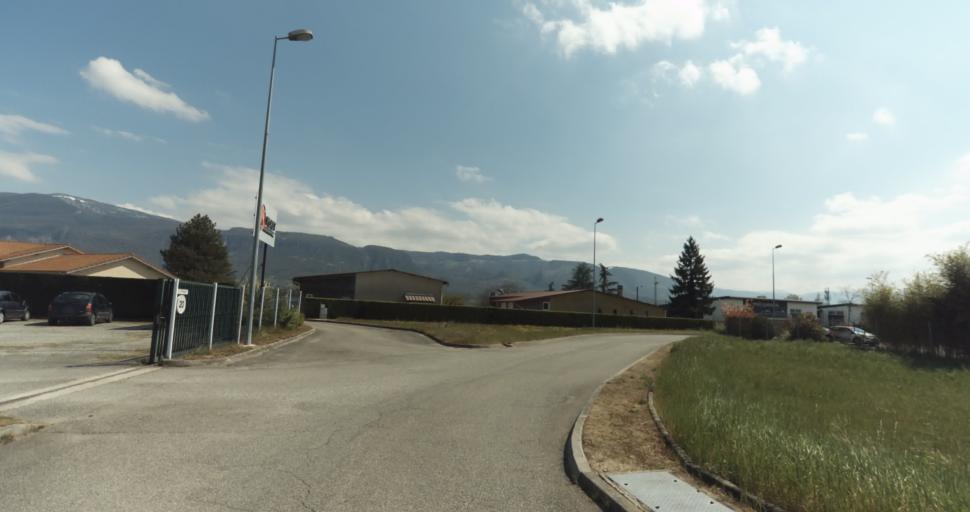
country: FR
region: Rhone-Alpes
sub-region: Departement de l'Isere
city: Saint-Marcellin
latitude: 45.1418
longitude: 5.3285
